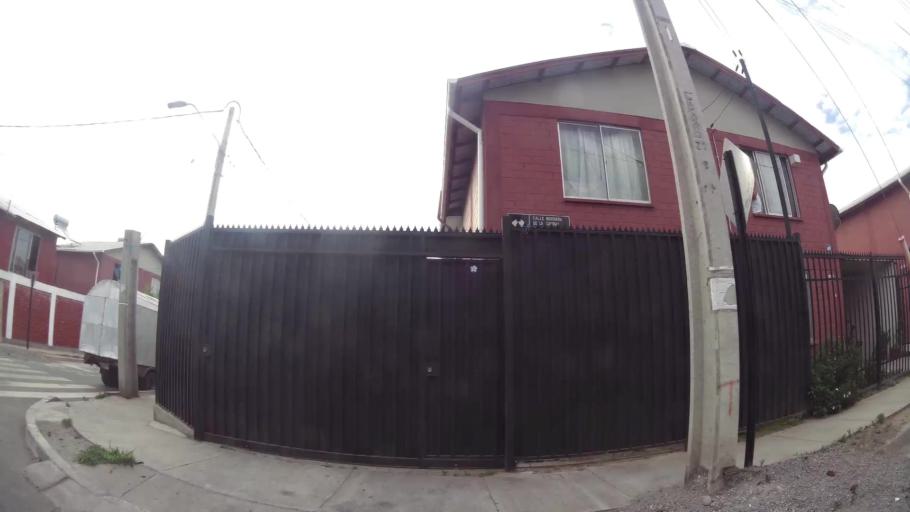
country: CL
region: Santiago Metropolitan
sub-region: Provincia de Cordillera
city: Puente Alto
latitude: -33.6298
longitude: -70.6043
